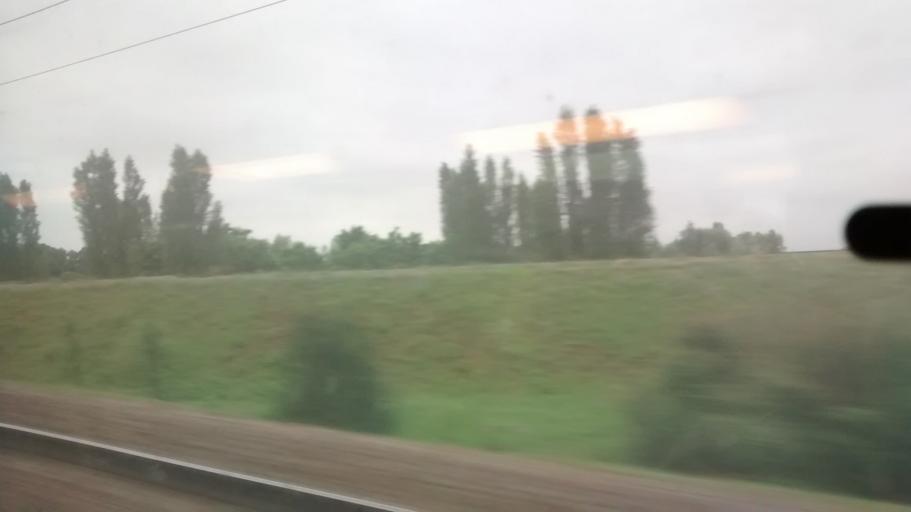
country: FR
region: Ile-de-France
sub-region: Departement de Seine-et-Marne
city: Saint-Germain-Laval
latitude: 48.3884
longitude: 2.9893
